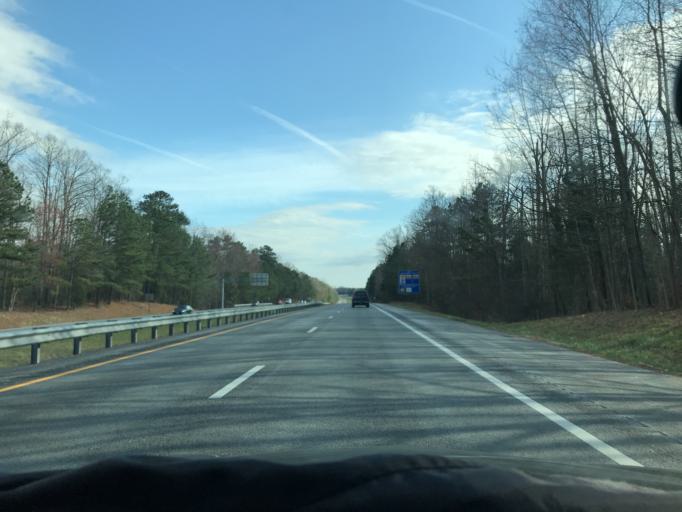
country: US
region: Virginia
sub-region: Chesterfield County
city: Brandermill
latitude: 37.4385
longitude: -77.6355
